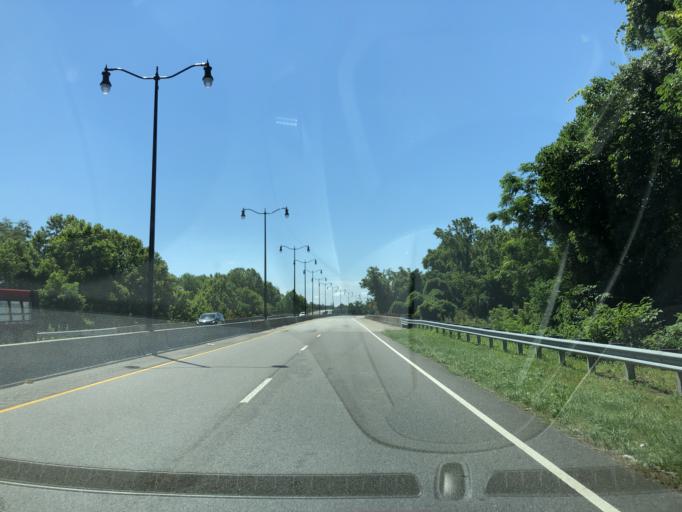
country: US
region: Georgia
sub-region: Richmond County
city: Augusta
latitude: 33.4871
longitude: -81.9897
